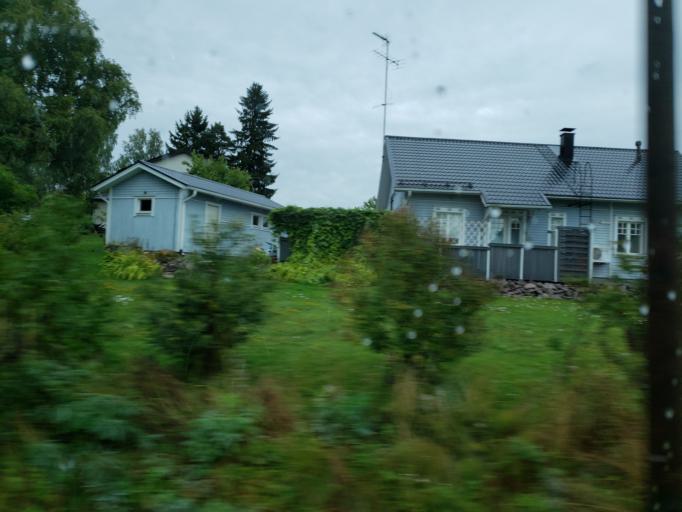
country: FI
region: Uusimaa
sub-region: Porvoo
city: Porvoo
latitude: 60.3646
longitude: 25.6242
